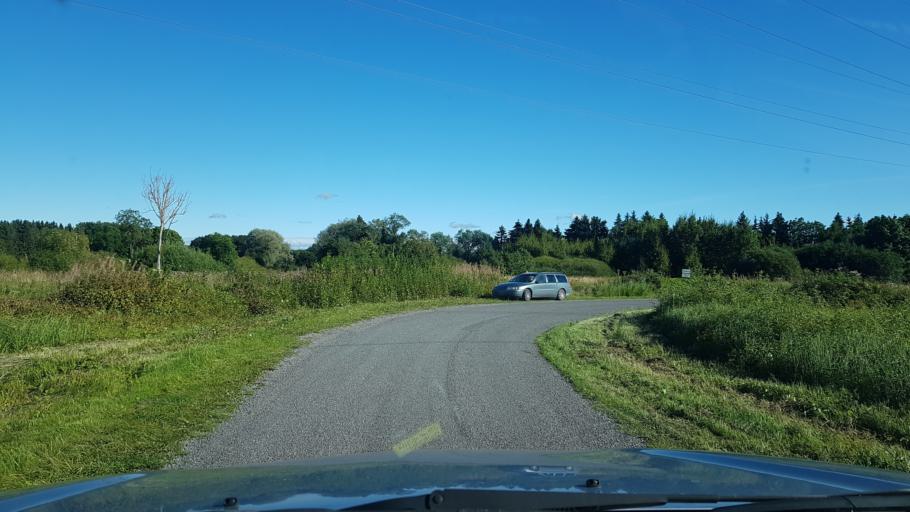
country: EE
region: Harju
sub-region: Joelaehtme vald
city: Loo
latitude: 59.4348
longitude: 24.9284
